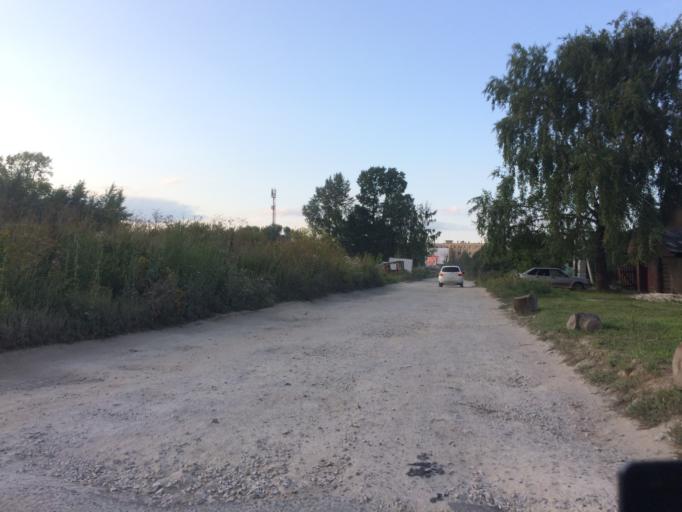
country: RU
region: Mariy-El
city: Medvedevo
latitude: 56.6514
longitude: 47.8384
